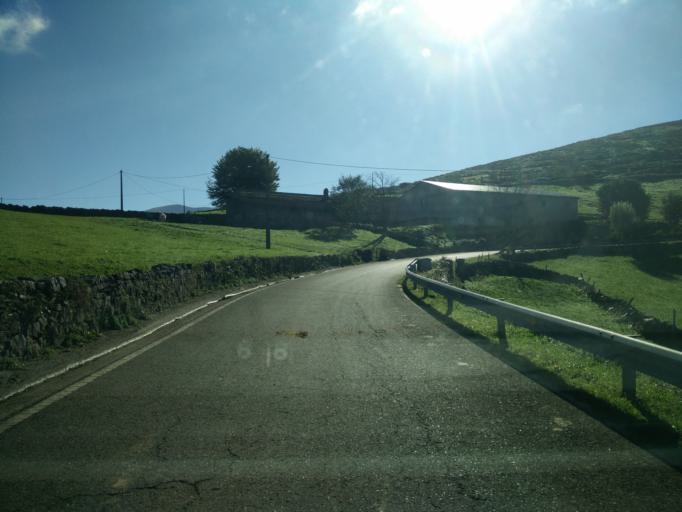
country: ES
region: Cantabria
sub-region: Provincia de Cantabria
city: San Pedro del Romeral
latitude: 43.1016
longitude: -3.8203
